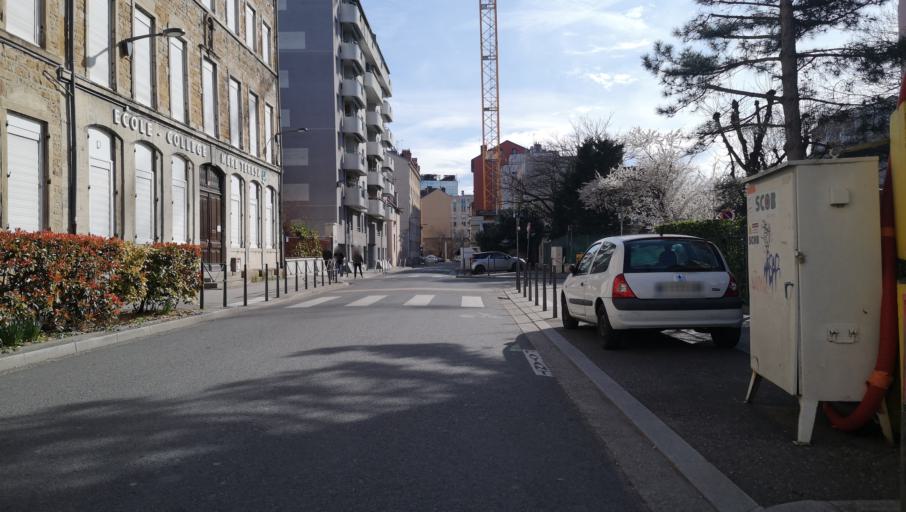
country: FR
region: Rhone-Alpes
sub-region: Departement du Rhone
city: Villeurbanne
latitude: 45.7740
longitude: 4.8698
